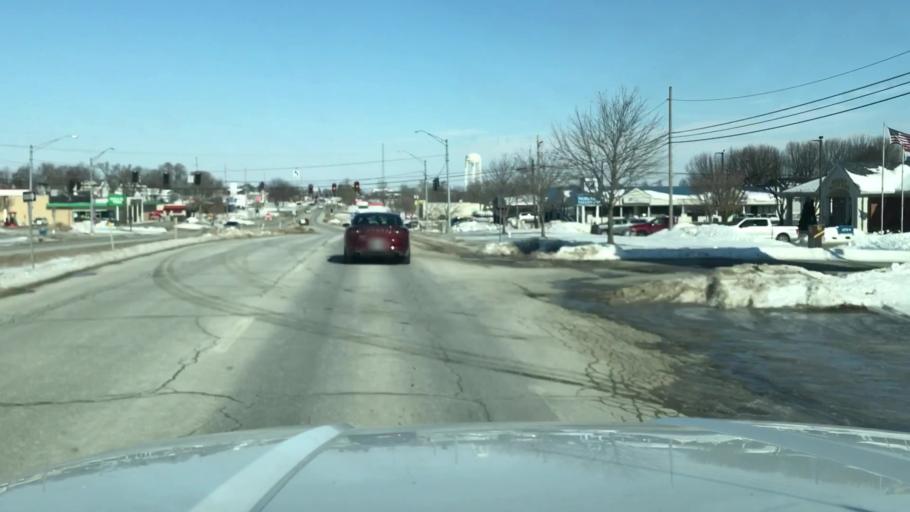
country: US
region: Missouri
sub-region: Andrew County
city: Savannah
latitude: 39.9383
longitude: -94.8218
